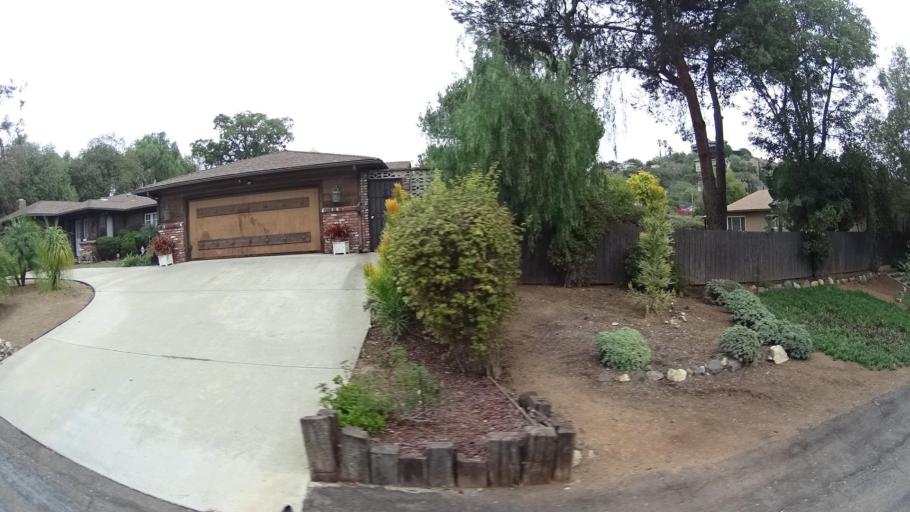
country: US
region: California
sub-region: San Diego County
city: Casa de Oro-Mount Helix
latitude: 32.7594
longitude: -116.9745
